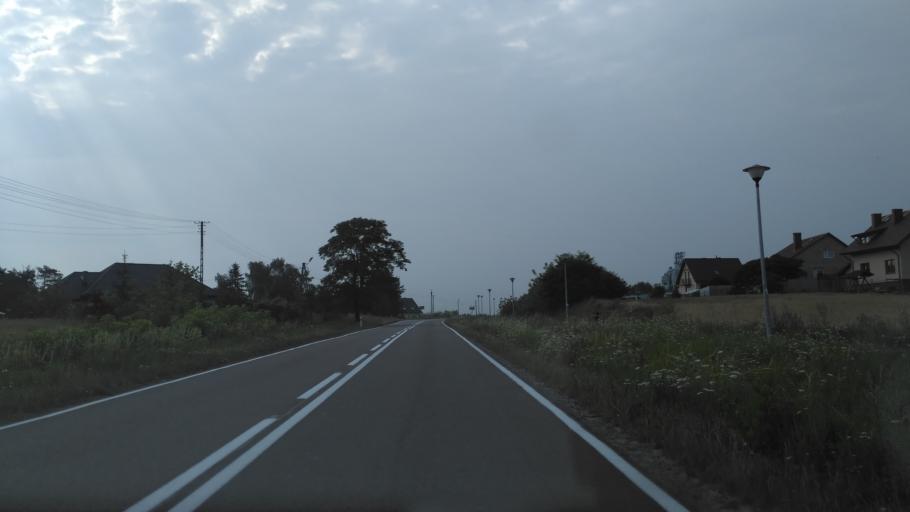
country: PL
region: Lublin Voivodeship
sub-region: Powiat chelmski
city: Rejowiec Fabryczny
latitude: 51.1858
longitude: 23.1705
